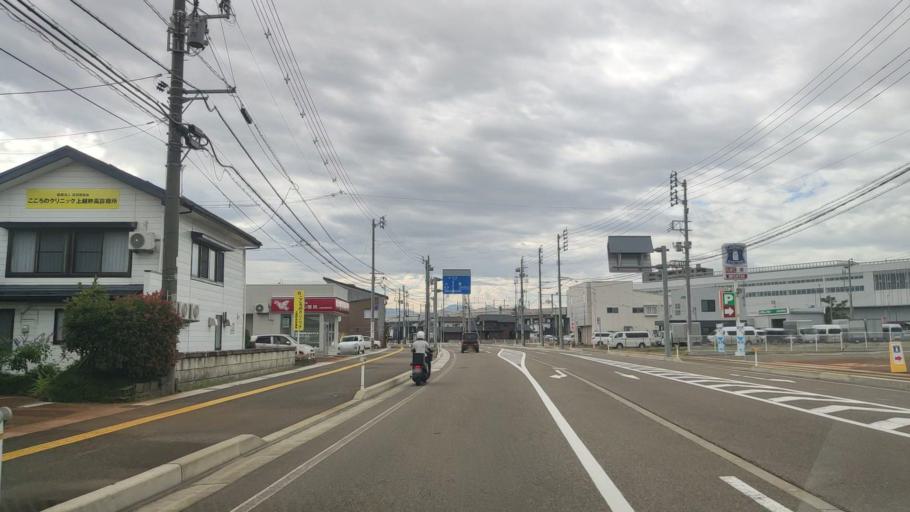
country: JP
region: Niigata
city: Joetsu
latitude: 37.0834
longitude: 138.2501
